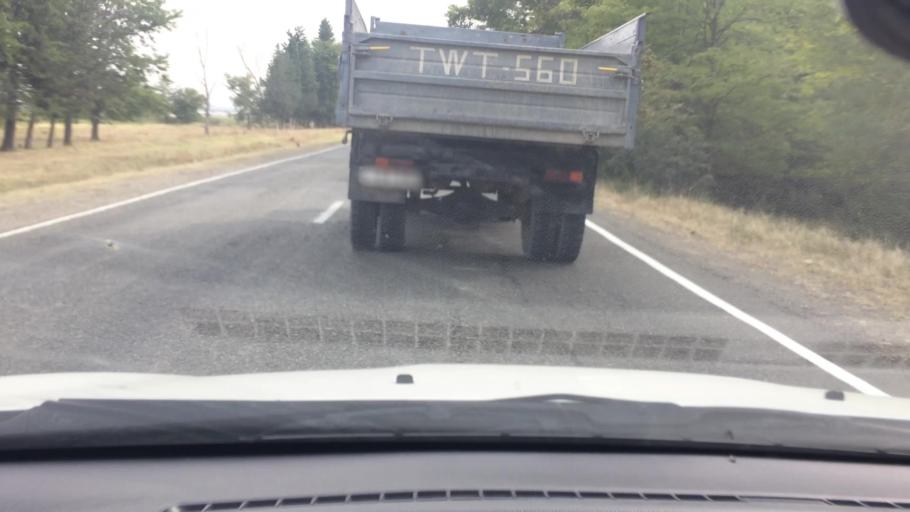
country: GE
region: Kvemo Kartli
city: Rust'avi
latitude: 41.4646
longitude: 44.9836
